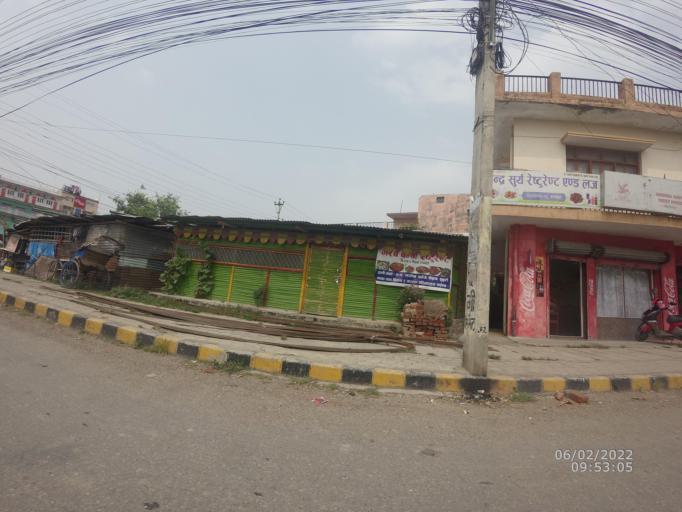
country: NP
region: Western Region
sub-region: Lumbini Zone
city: Bhairahawa
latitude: 27.5017
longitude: 83.4573
